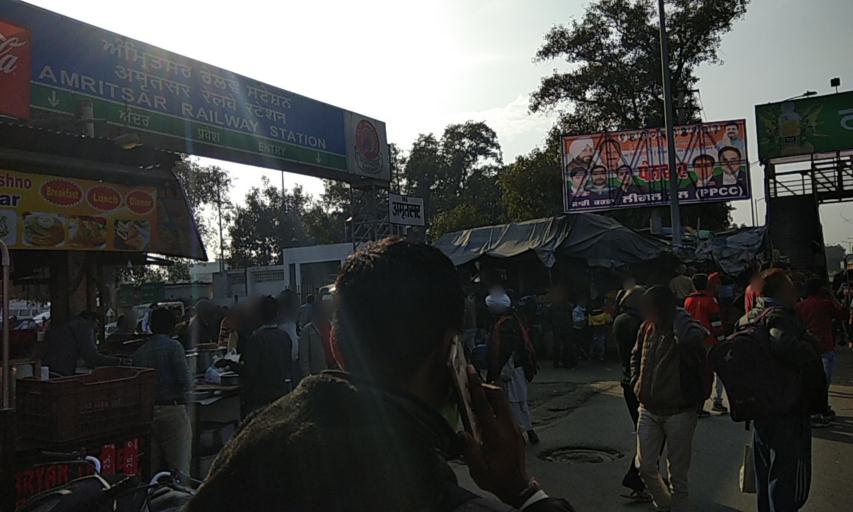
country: IN
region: Punjab
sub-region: Amritsar
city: Amritsar
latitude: 31.6344
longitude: 74.8680
